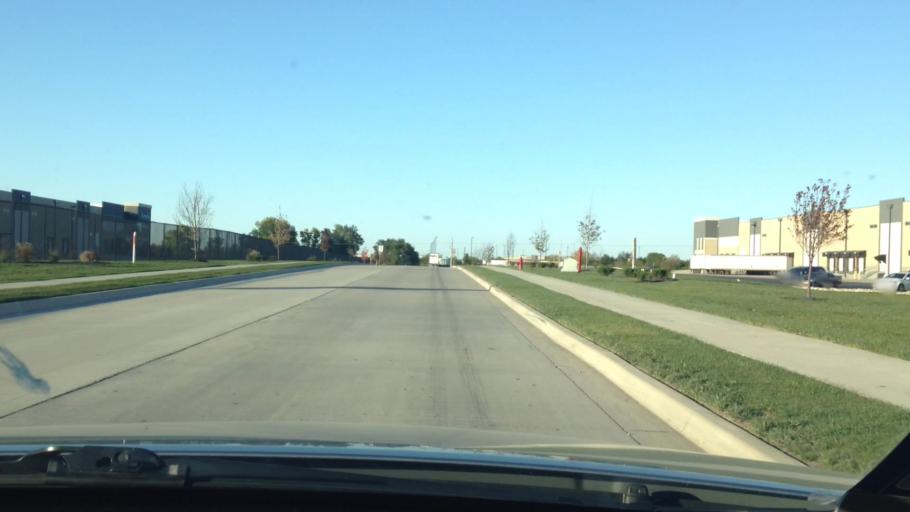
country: US
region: Kansas
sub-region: Johnson County
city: Gardner
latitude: 38.7789
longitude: -94.9423
